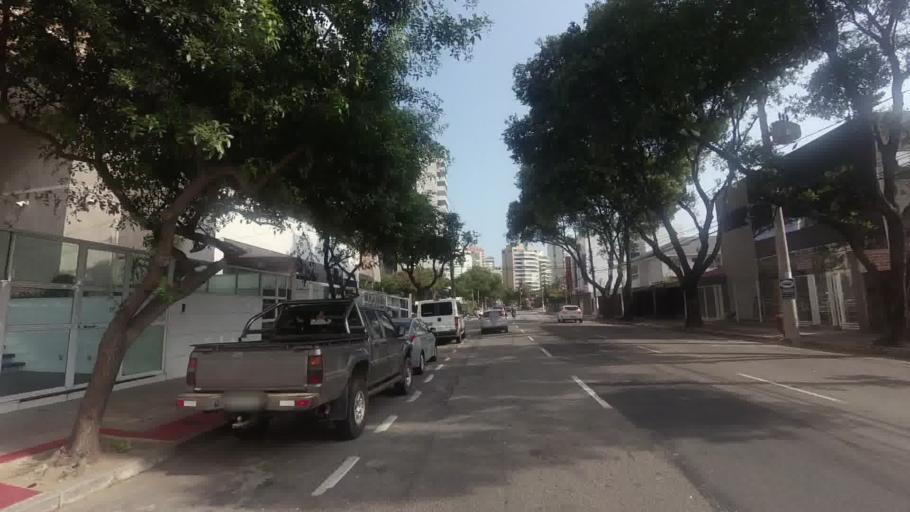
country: BR
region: Espirito Santo
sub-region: Vila Velha
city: Vila Velha
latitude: -20.3097
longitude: -40.2926
